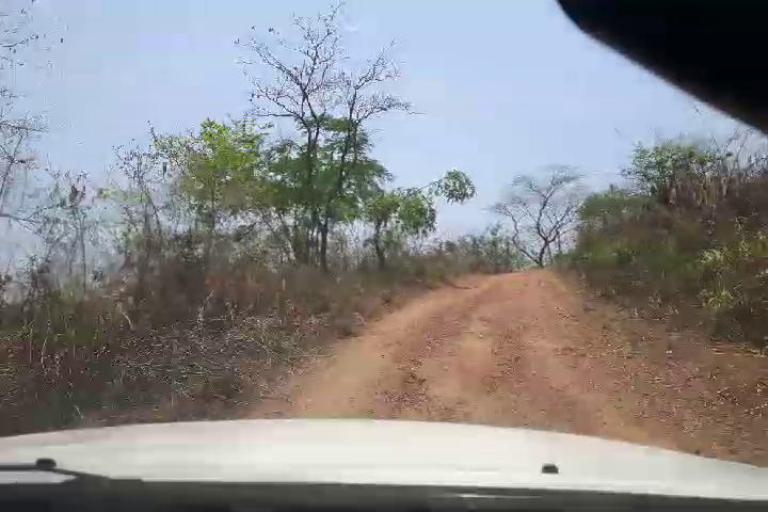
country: SL
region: Northern Province
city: Alikalia
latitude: 9.0754
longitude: -11.4761
